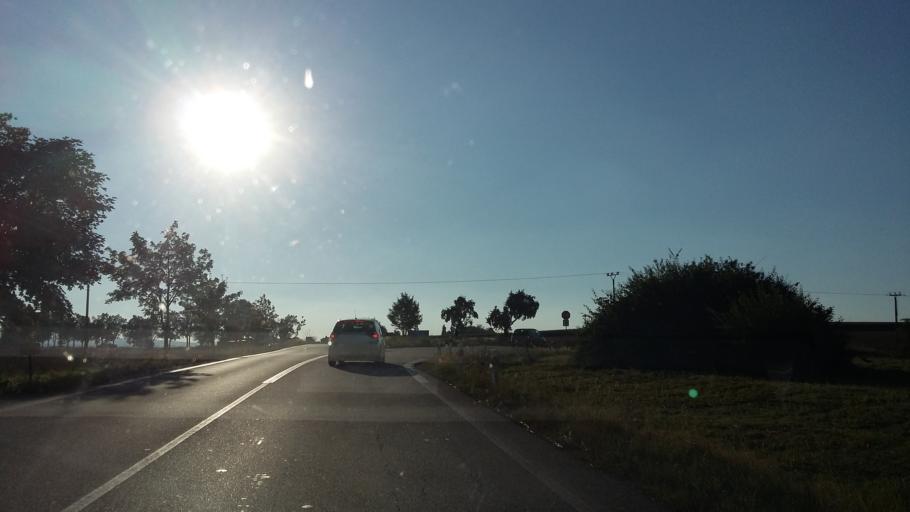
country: CZ
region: Vysocina
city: Velky Beranov
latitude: 49.4027
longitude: 15.6621
